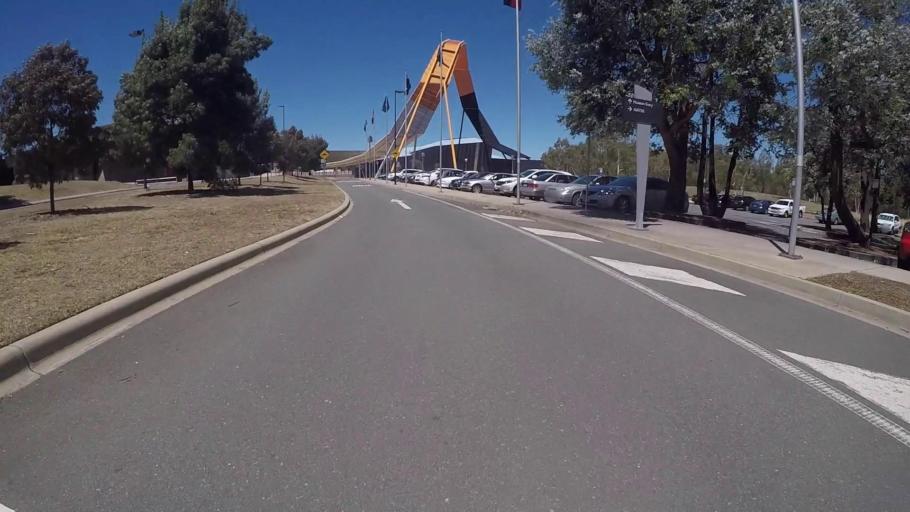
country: AU
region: Australian Capital Territory
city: Canberra
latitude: -35.2922
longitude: 149.1194
